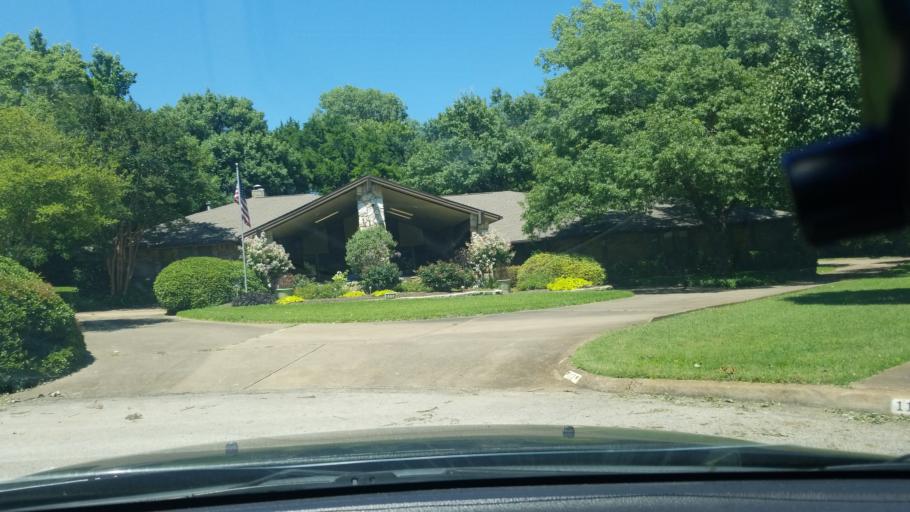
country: US
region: Texas
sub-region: Dallas County
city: Mesquite
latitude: 32.7529
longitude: -96.6035
